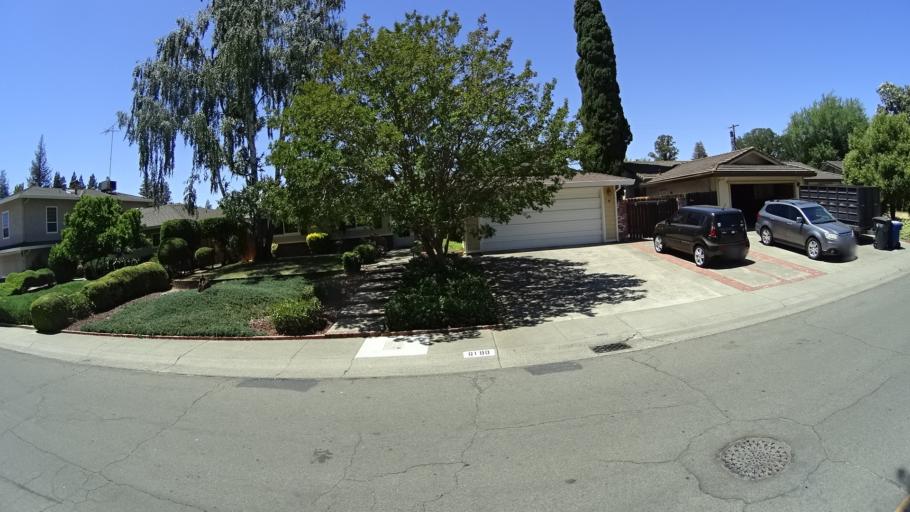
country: US
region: California
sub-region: Sacramento County
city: Parkway
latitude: 38.5127
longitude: -121.5078
